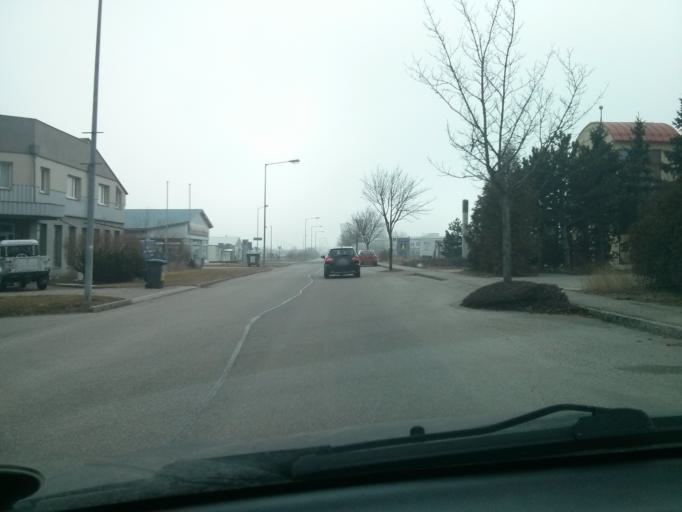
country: AT
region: Lower Austria
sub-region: Politischer Bezirk Wiener Neustadt
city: Theresienfeld
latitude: 47.8429
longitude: 16.2492
